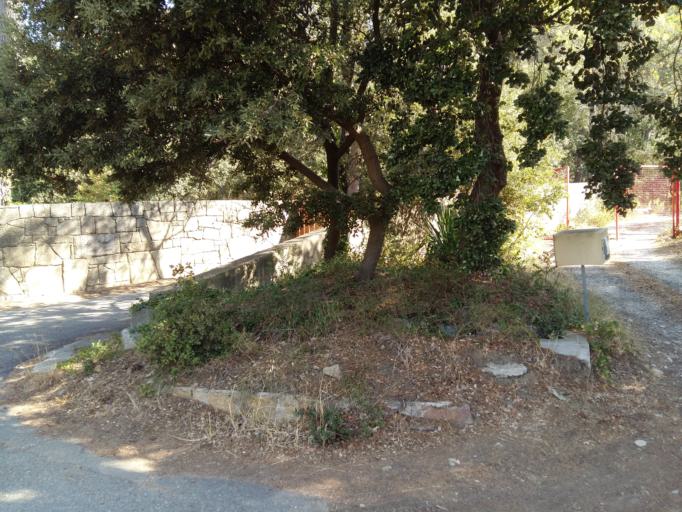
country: FR
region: Provence-Alpes-Cote d'Azur
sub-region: Departement du Vaucluse
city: Piolenc
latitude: 44.1682
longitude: 4.7760
